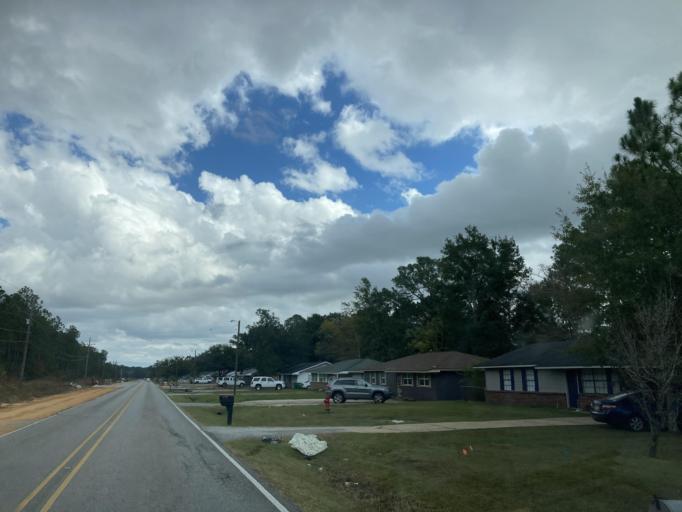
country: US
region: Mississippi
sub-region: Jackson County
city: Gulf Hills
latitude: 30.4390
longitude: -88.8243
